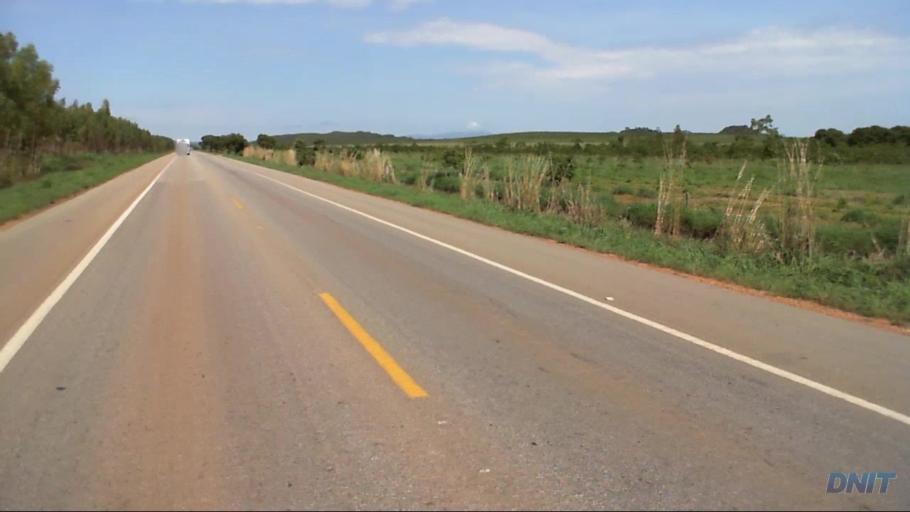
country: BR
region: Goias
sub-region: Barro Alto
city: Barro Alto
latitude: -15.2049
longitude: -48.7310
